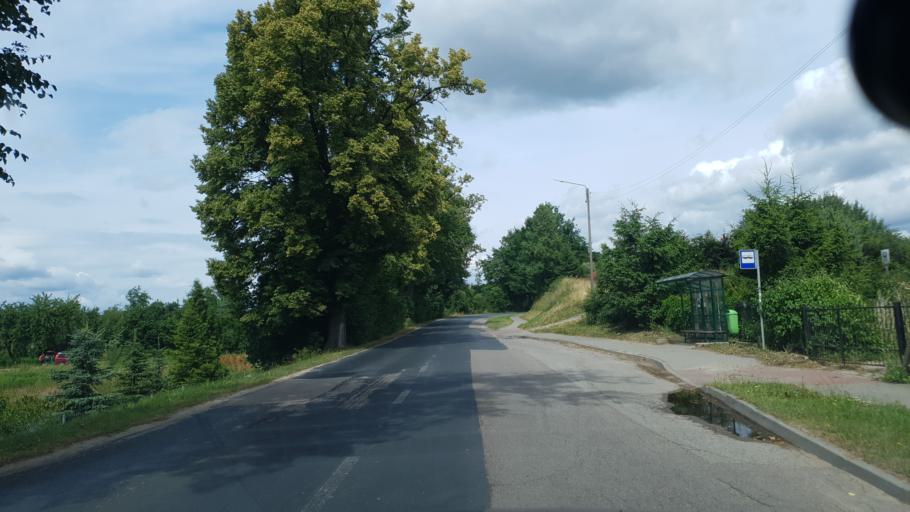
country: PL
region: Pomeranian Voivodeship
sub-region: Powiat kartuski
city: Chmielno
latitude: 54.2711
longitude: 18.0838
